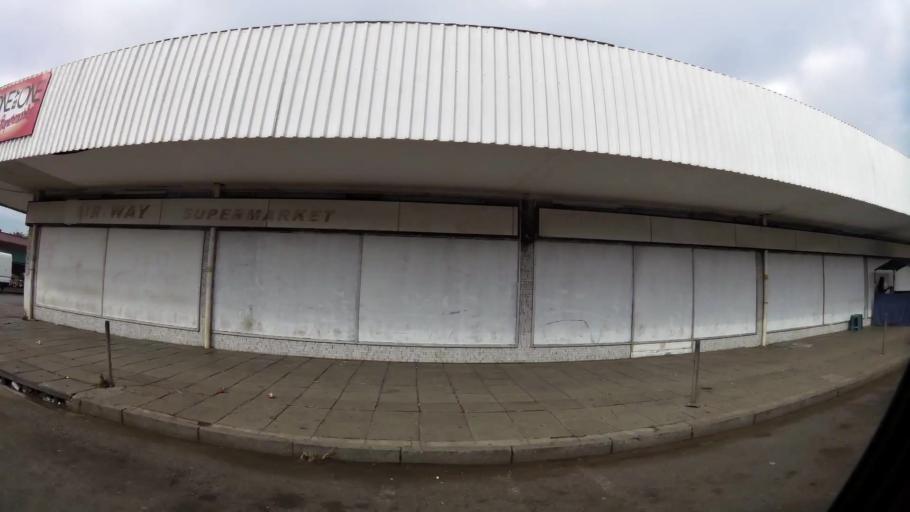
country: ZA
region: Gauteng
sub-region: Sedibeng District Municipality
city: Vanderbijlpark
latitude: -26.6965
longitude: 27.8373
